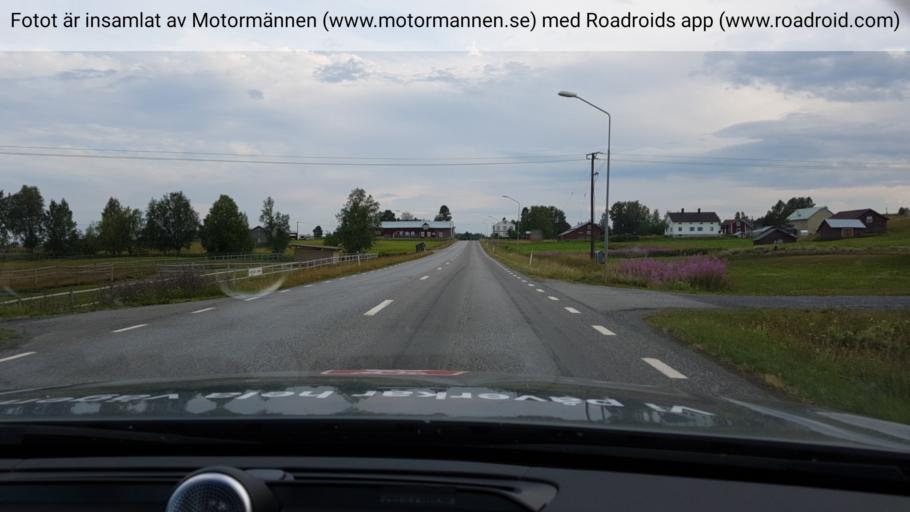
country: SE
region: Jaemtland
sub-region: Stroemsunds Kommun
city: Stroemsund
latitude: 63.5002
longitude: 15.2593
